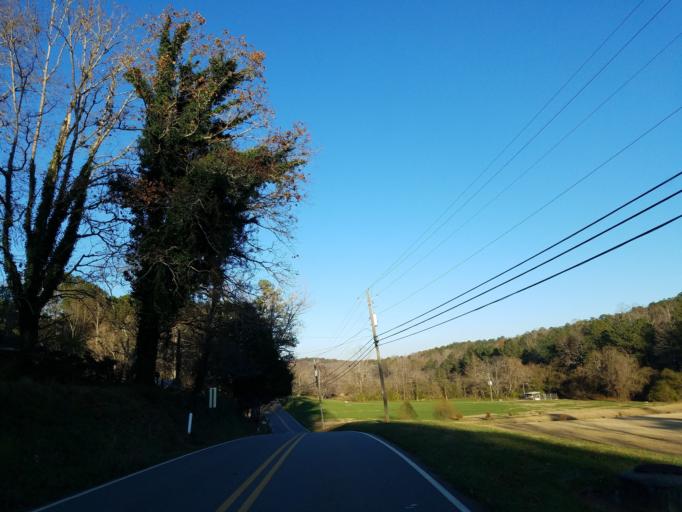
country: US
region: Georgia
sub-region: Cherokee County
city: Ball Ground
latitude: 34.3403
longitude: -84.3726
